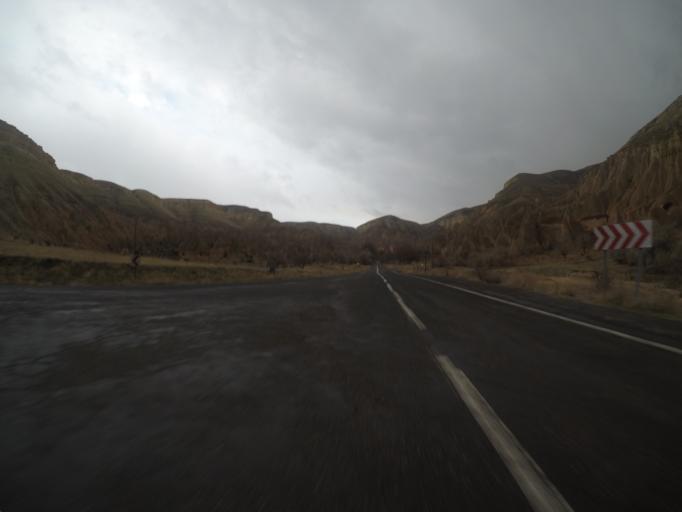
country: TR
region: Nevsehir
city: Goereme
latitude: 38.6729
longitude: 34.8627
